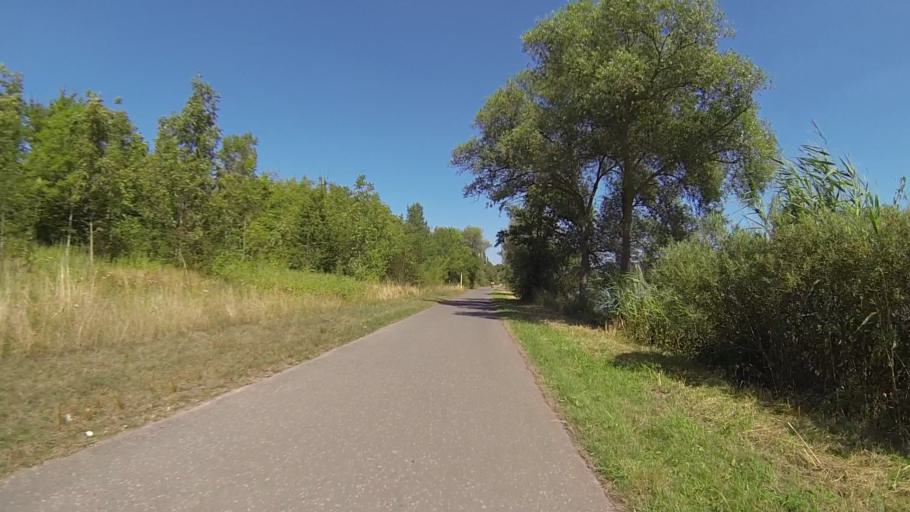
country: DE
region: Rheinland-Pfalz
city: Konz
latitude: 49.7087
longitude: 6.5764
